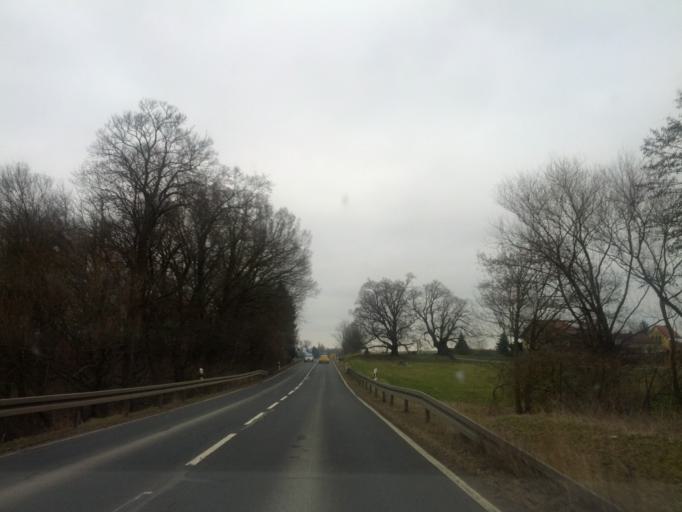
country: DE
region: Thuringia
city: Oberdorla
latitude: 51.1603
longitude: 10.4339
